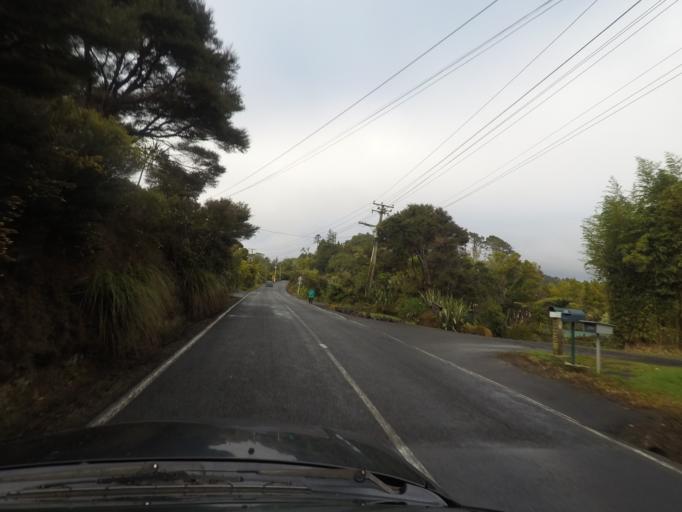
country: NZ
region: Auckland
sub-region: Auckland
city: Titirangi
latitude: -36.9246
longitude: 174.5830
